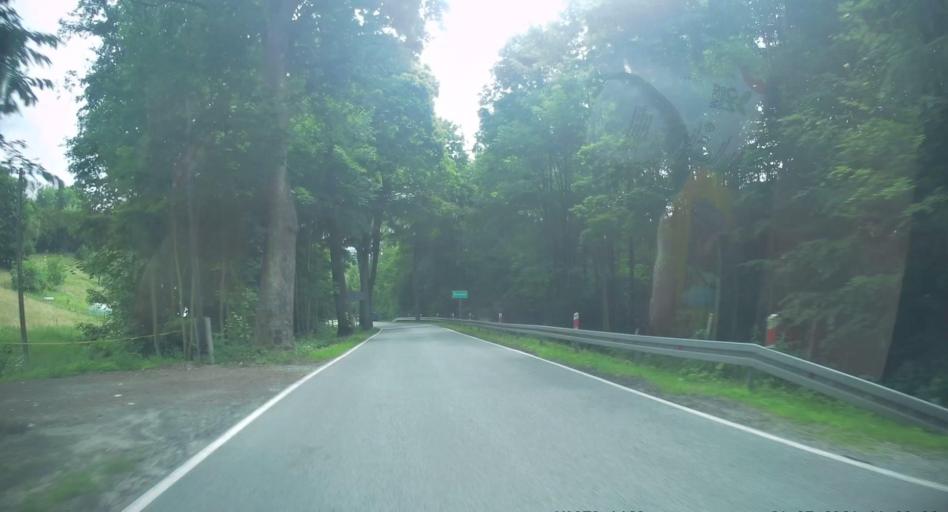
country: PL
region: Lower Silesian Voivodeship
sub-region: Powiat walbrzyski
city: Jedlina-Zdroj
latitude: 50.7311
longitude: 16.3679
